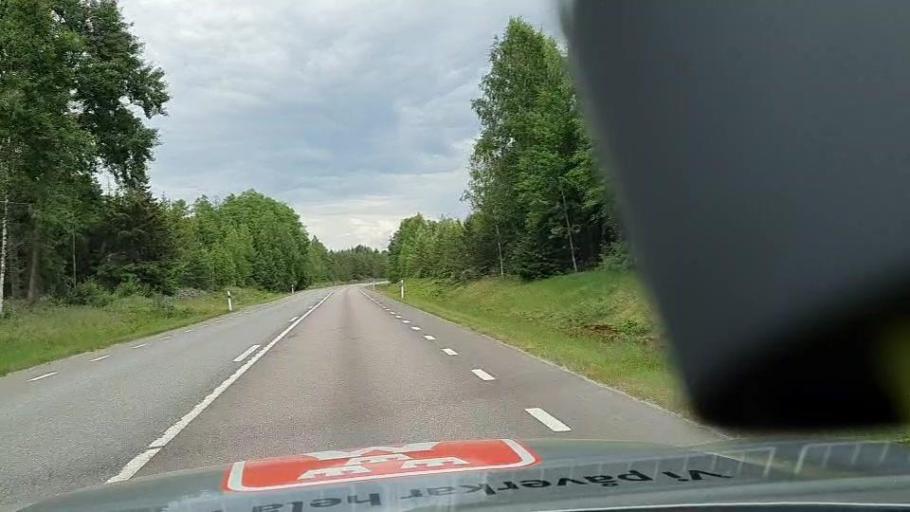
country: SE
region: Kalmar
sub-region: Emmaboda Kommun
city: Emmaboda
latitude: 56.4487
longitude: 15.5639
